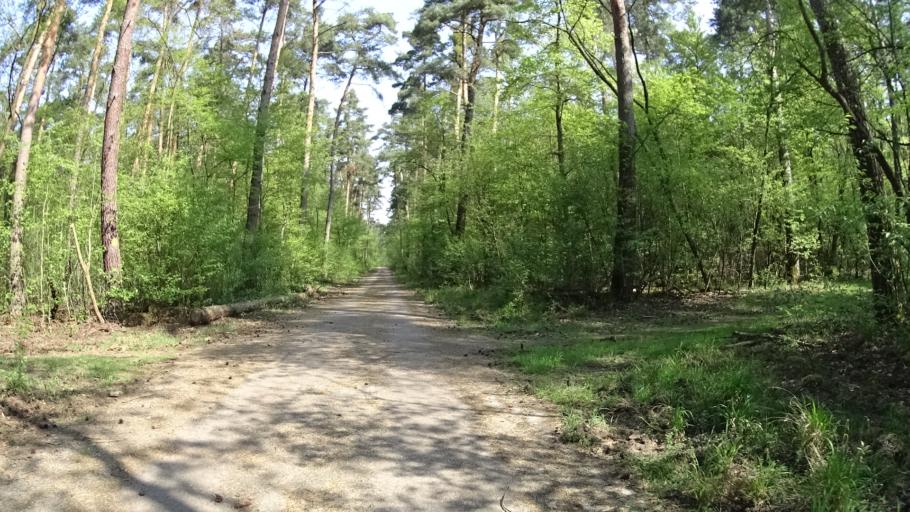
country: DE
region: Hesse
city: Viernheim
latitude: 49.5428
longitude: 8.5242
